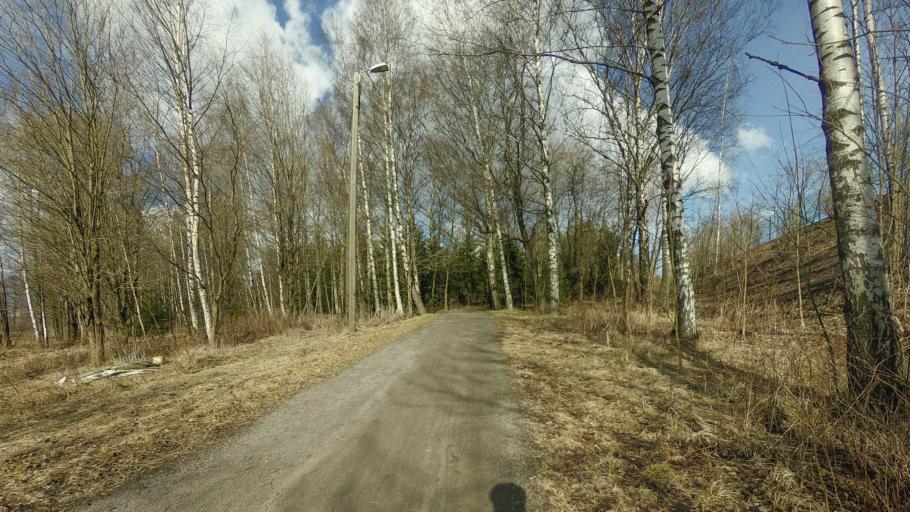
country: FI
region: Uusimaa
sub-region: Helsinki
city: Helsinki
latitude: 60.1929
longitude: 25.0231
